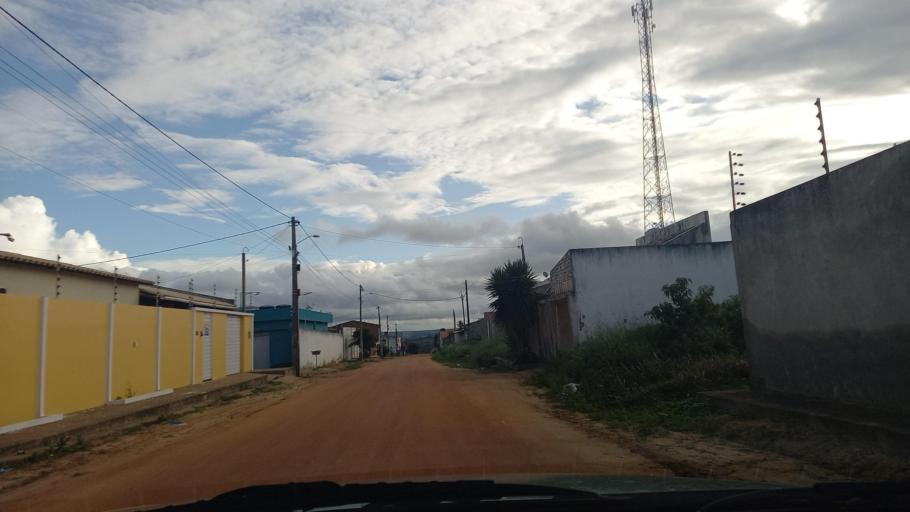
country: BR
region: Pernambuco
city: Garanhuns
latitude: -8.9146
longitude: -36.4790
